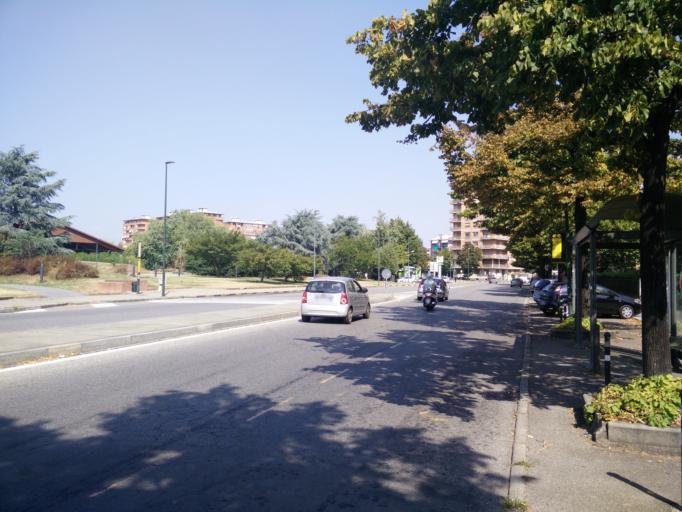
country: IT
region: Piedmont
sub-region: Provincia di Torino
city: Nichelino
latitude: 45.0161
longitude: 7.6484
